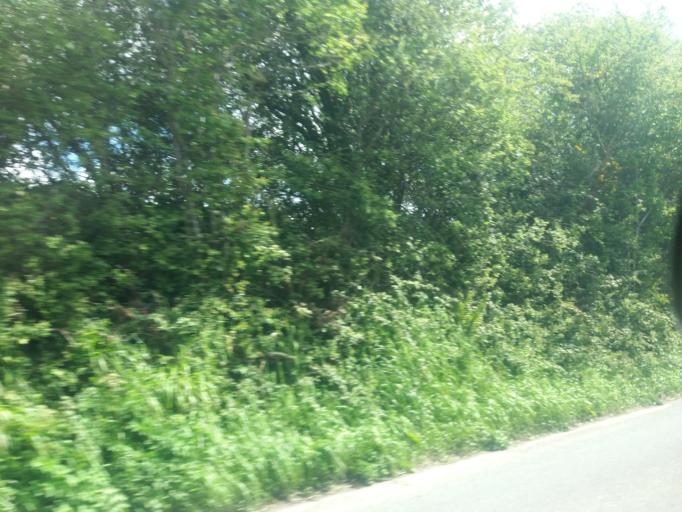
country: IE
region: Leinster
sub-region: Loch Garman
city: New Ross
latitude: 52.2671
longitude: -6.7720
